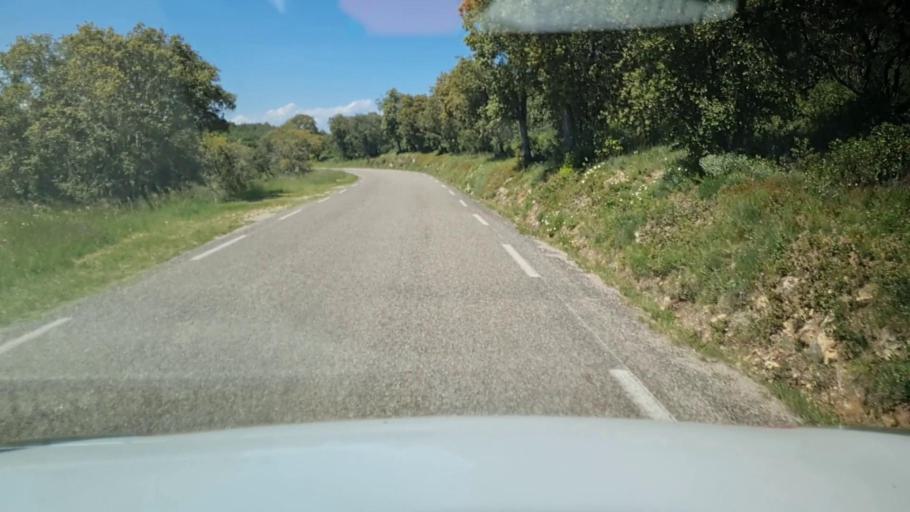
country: FR
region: Languedoc-Roussillon
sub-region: Departement du Gard
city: Clarensac
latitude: 43.8535
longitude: 4.2167
